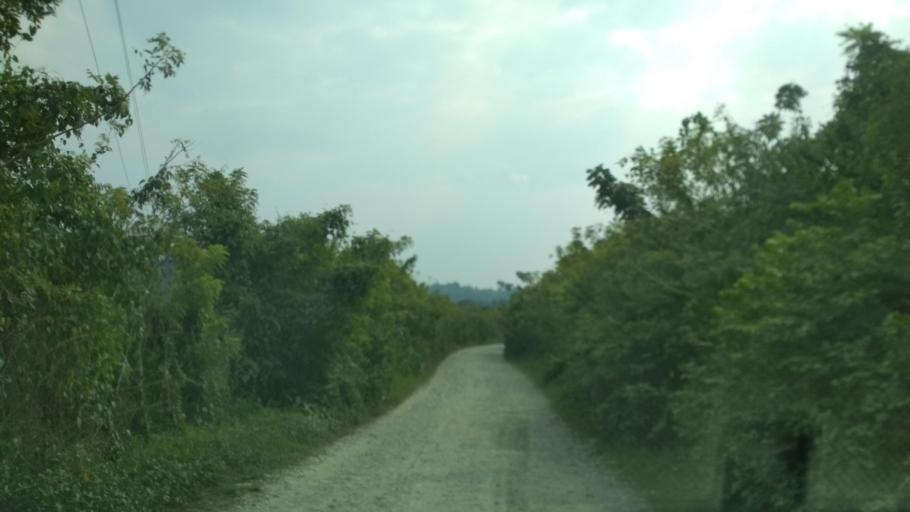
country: MM
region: Kayah
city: Loikaw
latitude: 20.2345
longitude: 97.2783
